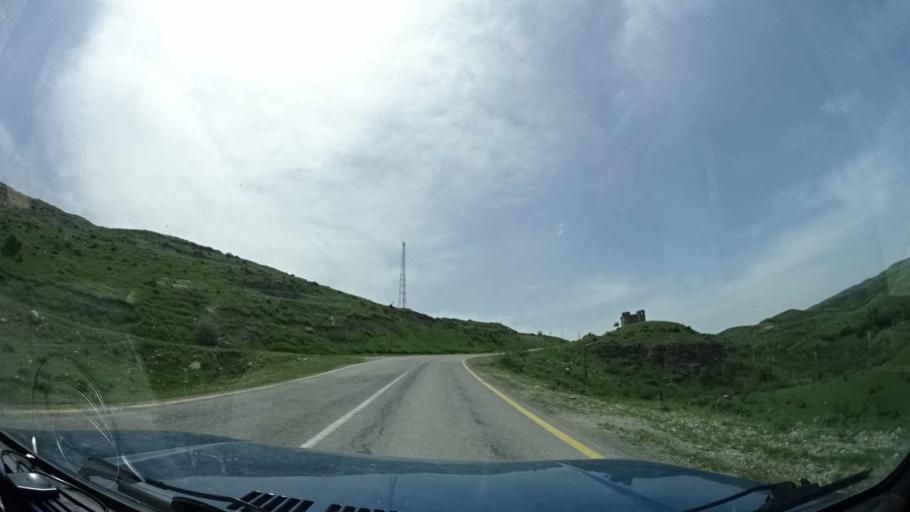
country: AZ
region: Xizi
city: Khyzy
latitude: 40.9045
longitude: 49.1143
